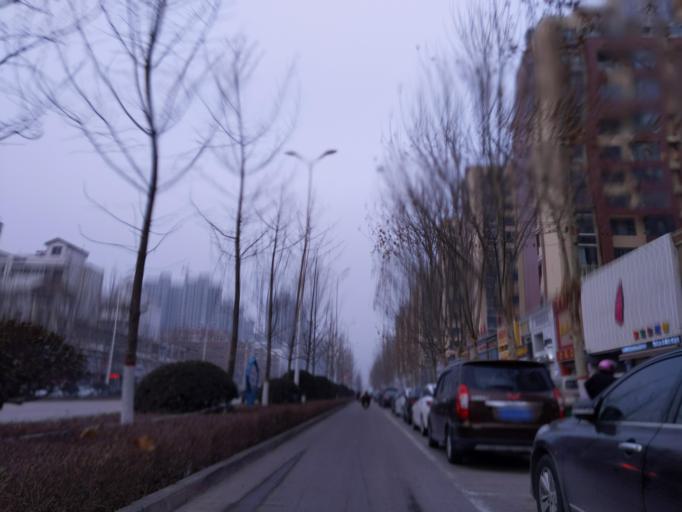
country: CN
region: Henan Sheng
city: Puyang
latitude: 35.7831
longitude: 115.0267
